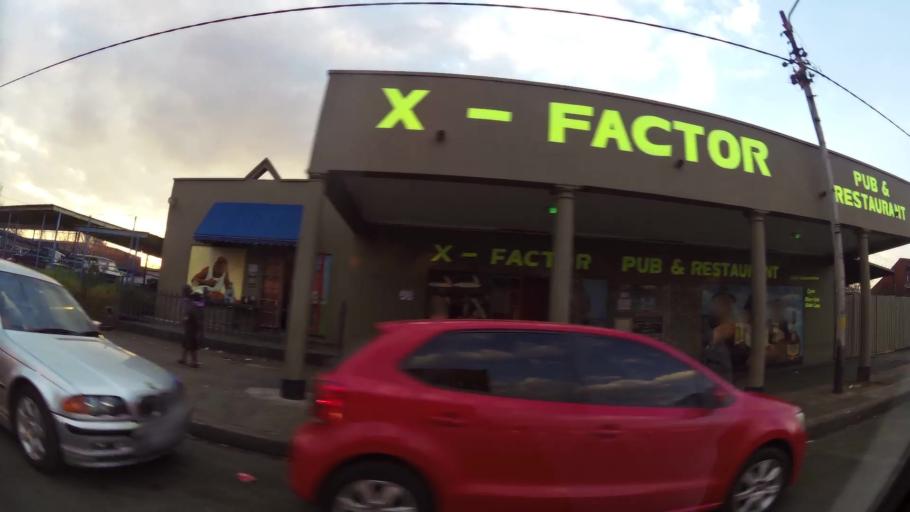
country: ZA
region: Gauteng
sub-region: Ekurhuleni Metropolitan Municipality
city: Germiston
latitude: -26.1877
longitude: 28.1646
